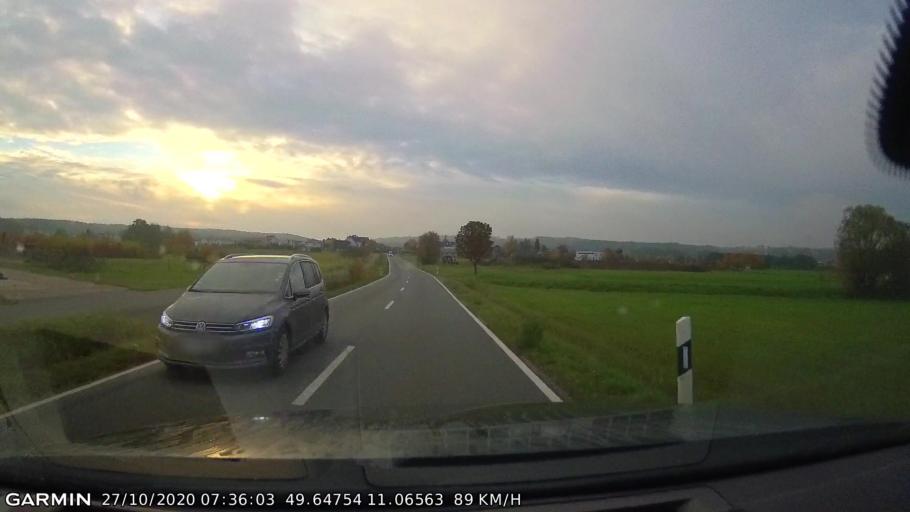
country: DE
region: Bavaria
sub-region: Upper Franconia
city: Langensendelbach
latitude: 49.6473
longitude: 11.0659
